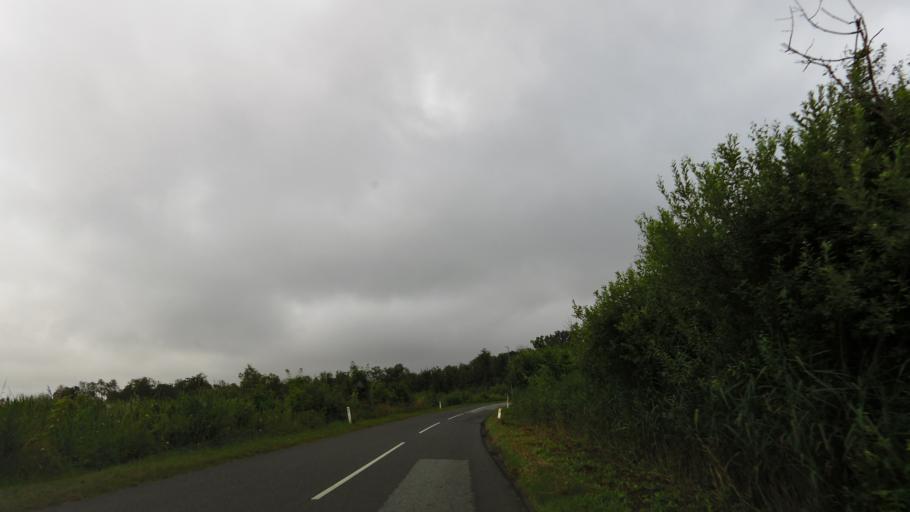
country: DK
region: South Denmark
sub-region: Nordfyns Kommune
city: Otterup
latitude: 55.5681
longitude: 10.3904
